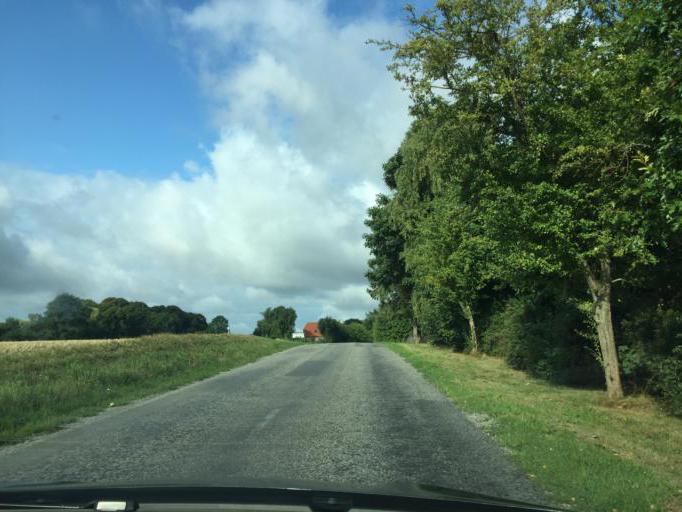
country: DK
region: South Denmark
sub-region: Faaborg-Midtfyn Kommune
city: Faaborg
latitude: 55.1957
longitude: 10.2528
